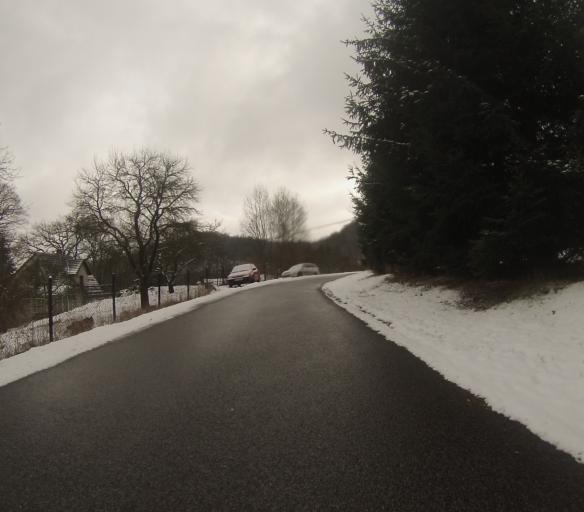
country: CZ
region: Ustecky
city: Benesov nad Ploucnici
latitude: 50.7383
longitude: 14.2645
